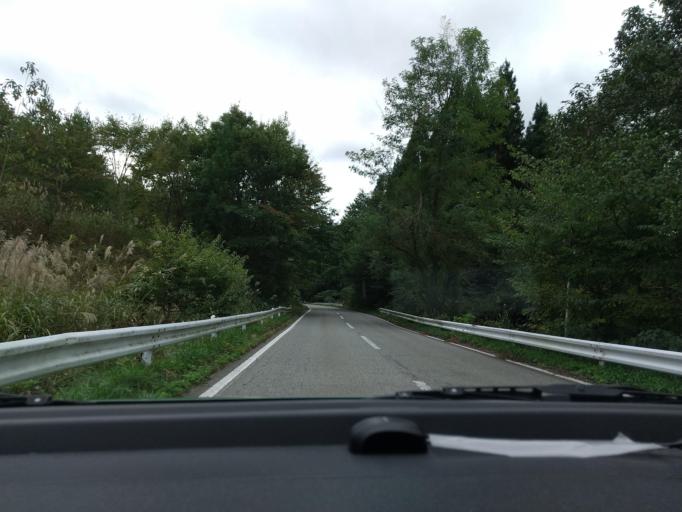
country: JP
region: Akita
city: Kakunodatemachi
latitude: 39.5493
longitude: 140.6337
